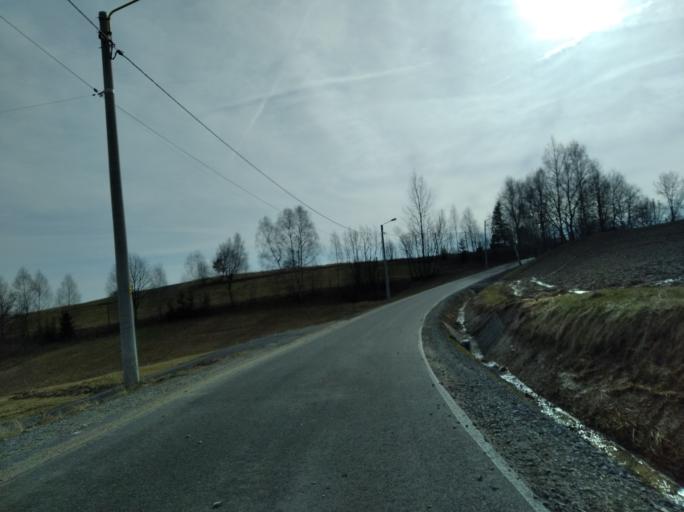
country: PL
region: Subcarpathian Voivodeship
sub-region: Powiat brzozowski
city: Jasienica Rosielna
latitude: 49.7646
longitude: 21.9444
